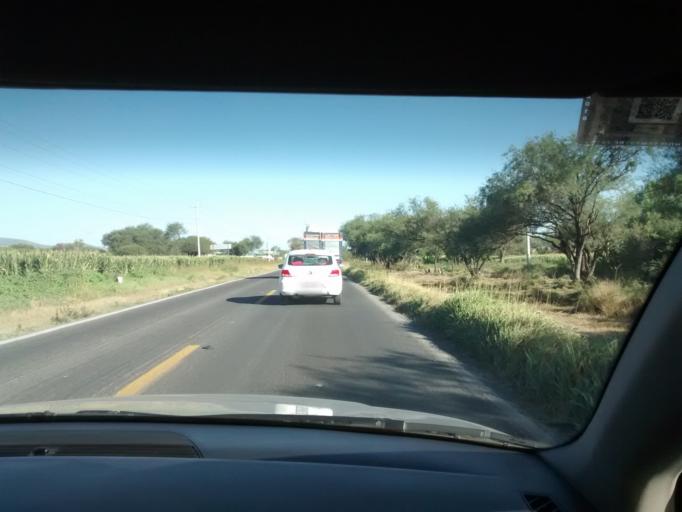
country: MX
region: Puebla
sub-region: Tehuacan
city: Magdalena Cuayucatepec
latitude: 18.5221
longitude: -97.5088
